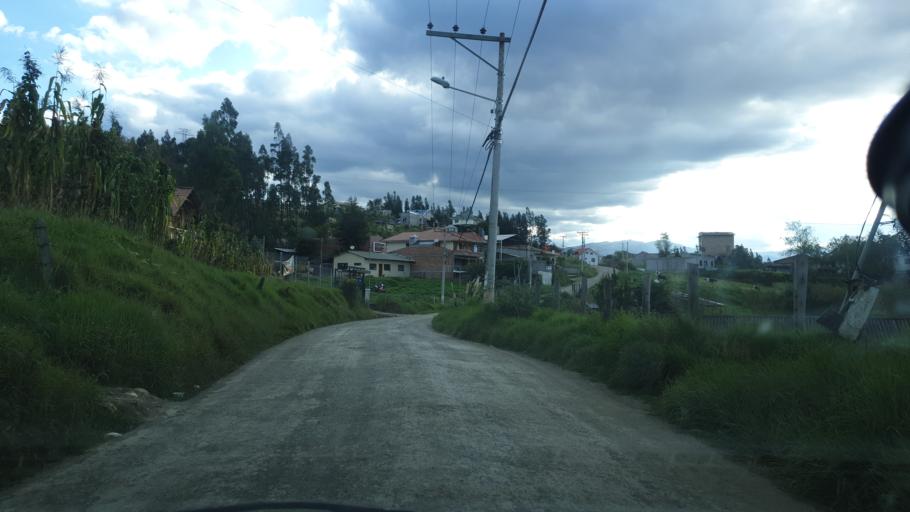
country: EC
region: Azuay
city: Cuenca
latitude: -2.9246
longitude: -78.9694
